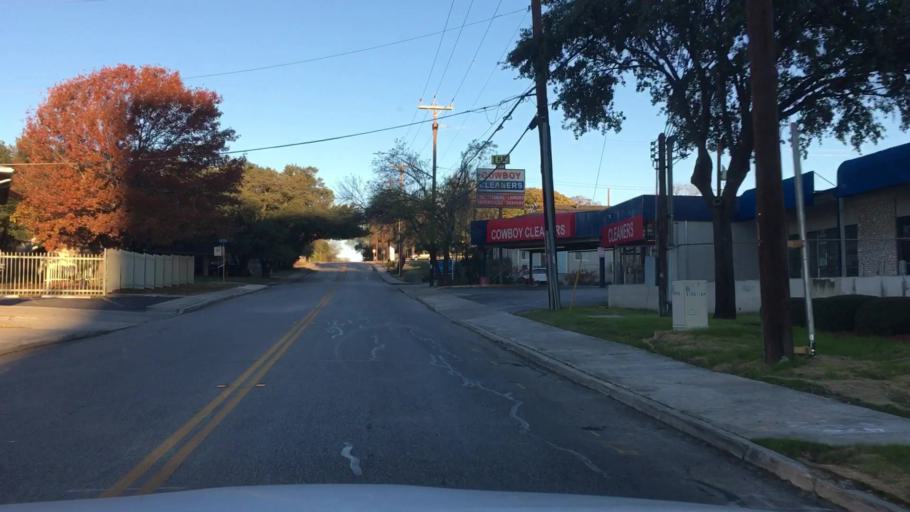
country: US
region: Texas
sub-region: Bexar County
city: Castle Hills
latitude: 29.5318
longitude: -98.4971
